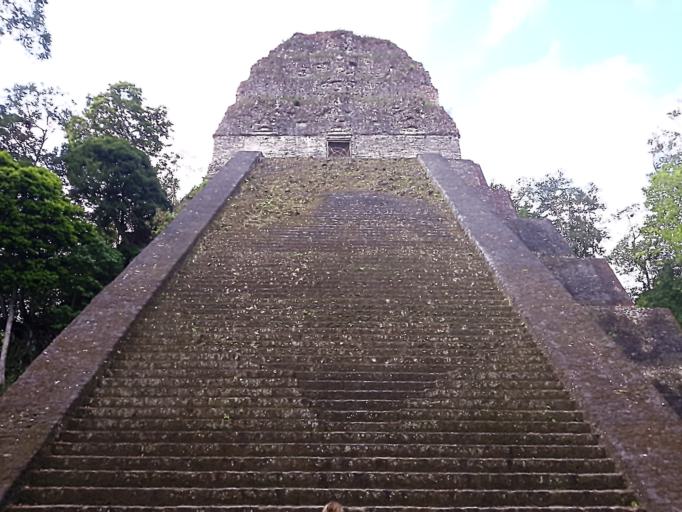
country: GT
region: Peten
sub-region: Municipio de San Jose
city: San Jose
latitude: 17.2199
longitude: -89.6236
